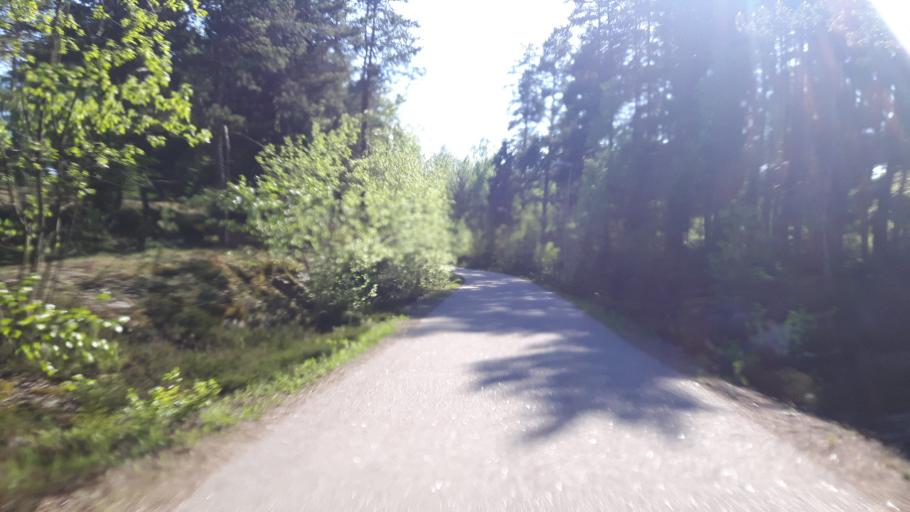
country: FI
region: Kymenlaakso
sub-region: Kotka-Hamina
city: Kotka
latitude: 60.4459
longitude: 26.8912
